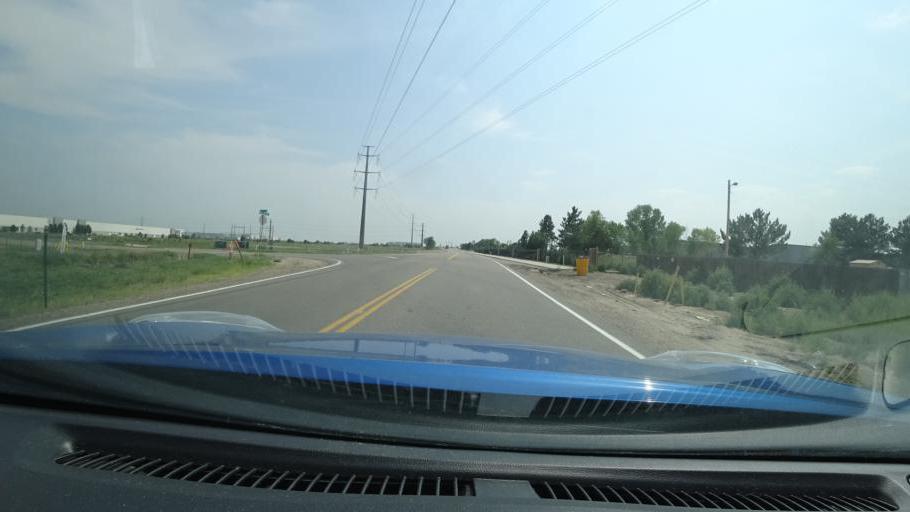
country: US
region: Colorado
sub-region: Adams County
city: Aurora
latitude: 39.7550
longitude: -104.7347
